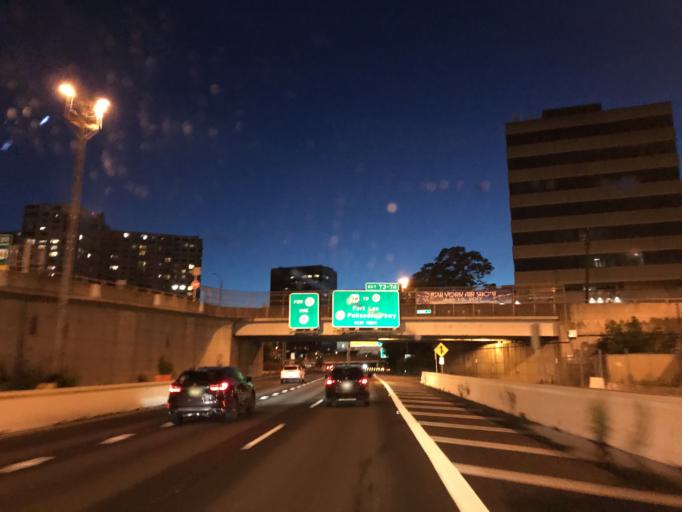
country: US
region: New Jersey
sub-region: Bergen County
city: Fort Lee
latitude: 40.8555
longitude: -73.9695
